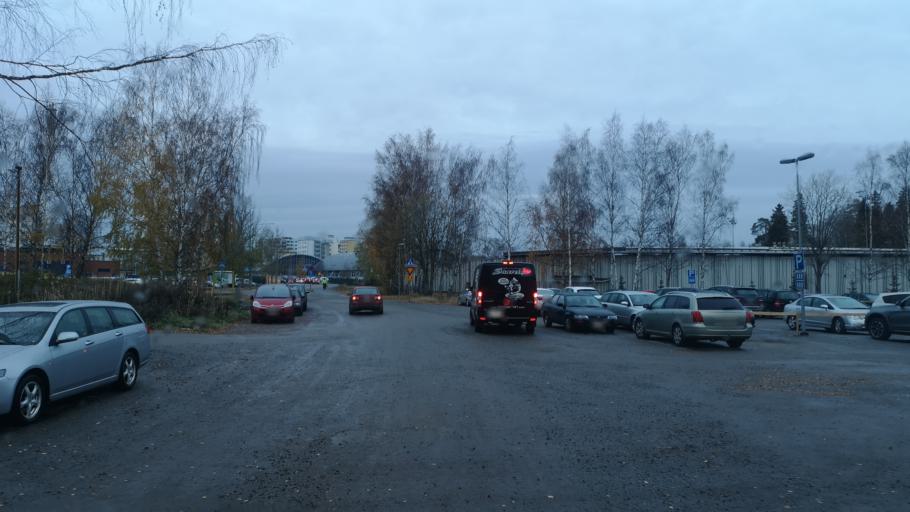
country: FI
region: Ostrobothnia
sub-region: Vaasa
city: Vaasa
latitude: 63.0834
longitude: 21.6201
